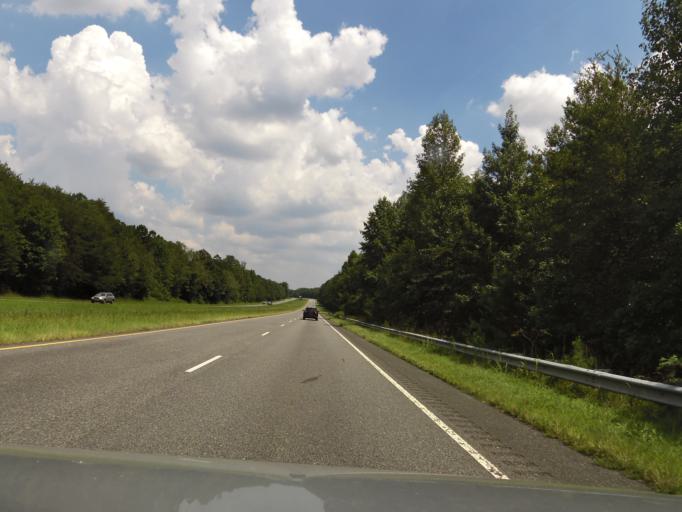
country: US
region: North Carolina
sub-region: Polk County
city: Columbus
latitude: 35.2703
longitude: -82.1486
